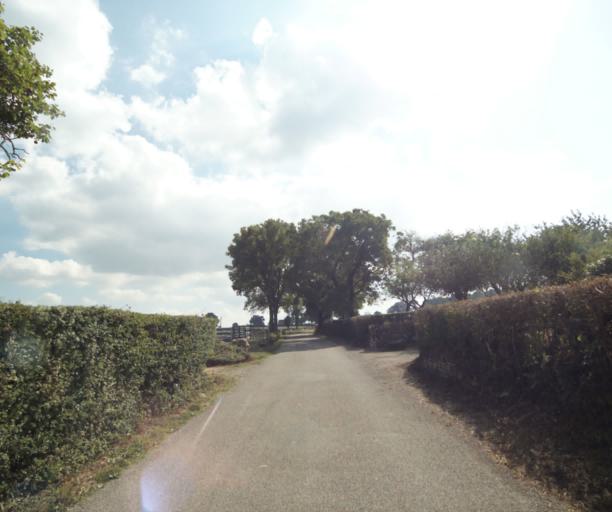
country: FR
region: Bourgogne
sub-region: Departement de Saone-et-Loire
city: Charolles
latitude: 46.3600
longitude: 4.2350
